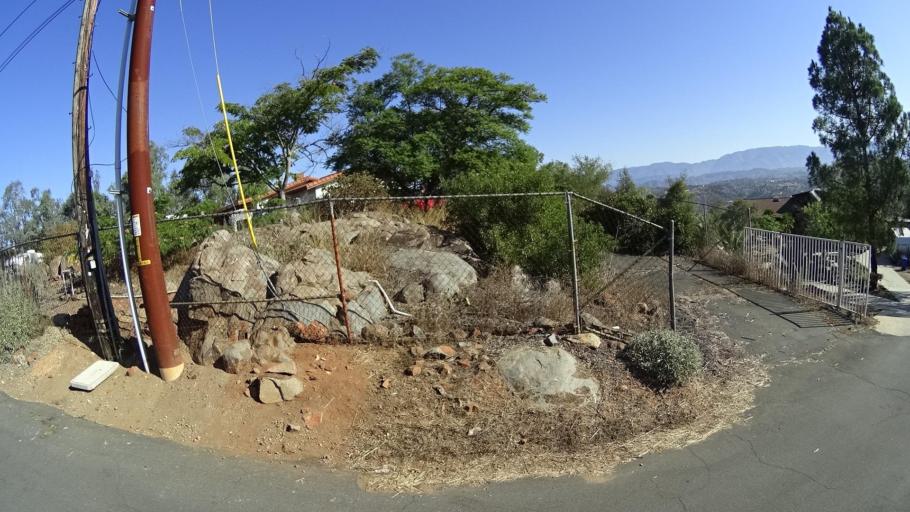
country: US
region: California
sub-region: San Diego County
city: Hidden Meadows
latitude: 33.2373
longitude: -117.1178
